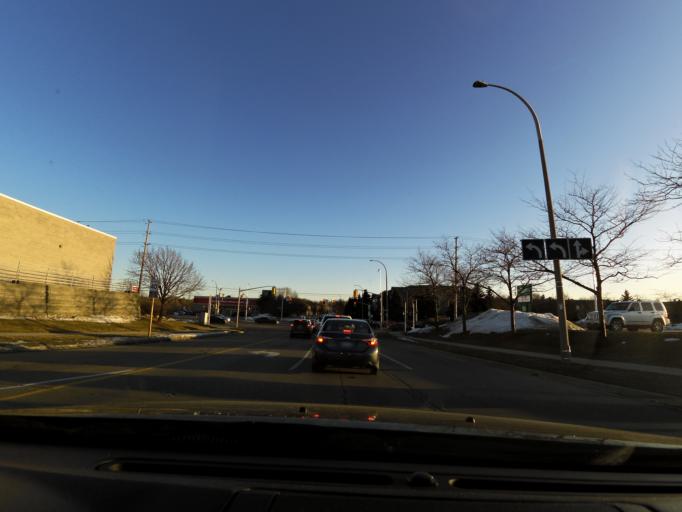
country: CA
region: Ontario
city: Ancaster
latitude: 43.2280
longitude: -79.9425
